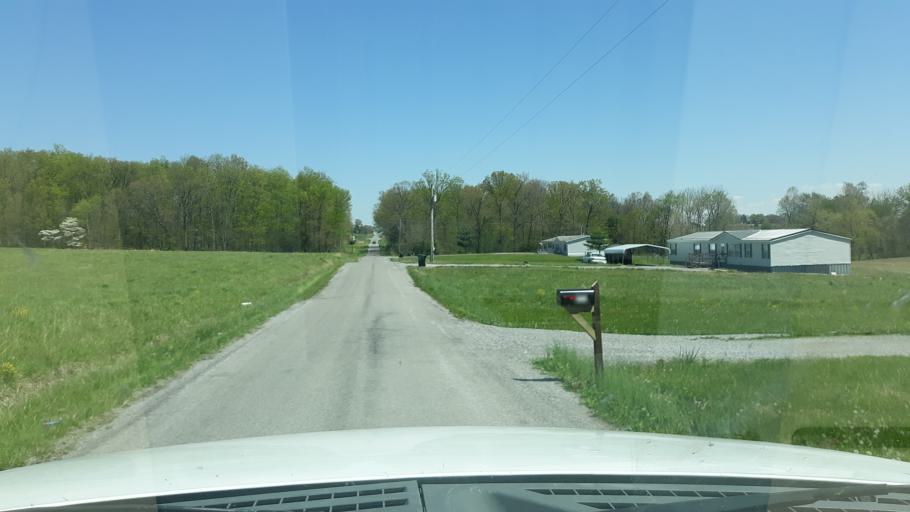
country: US
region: Illinois
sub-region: Saline County
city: Harrisburg
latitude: 37.8849
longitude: -88.6582
